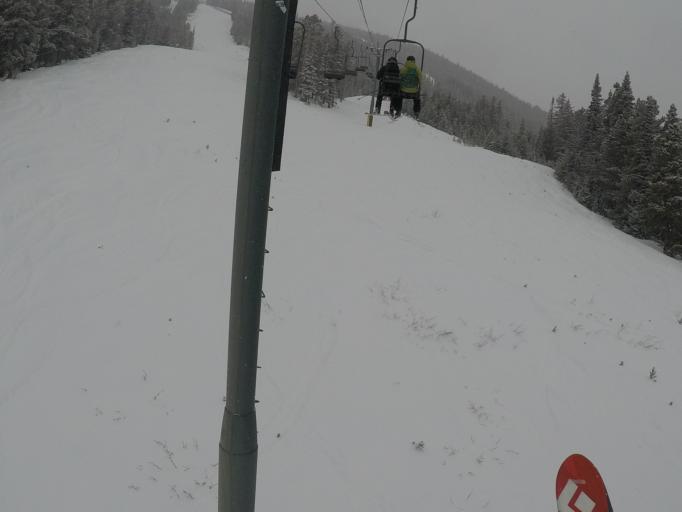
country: US
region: Montana
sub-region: Carbon County
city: Red Lodge
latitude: 45.1875
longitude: -109.3483
